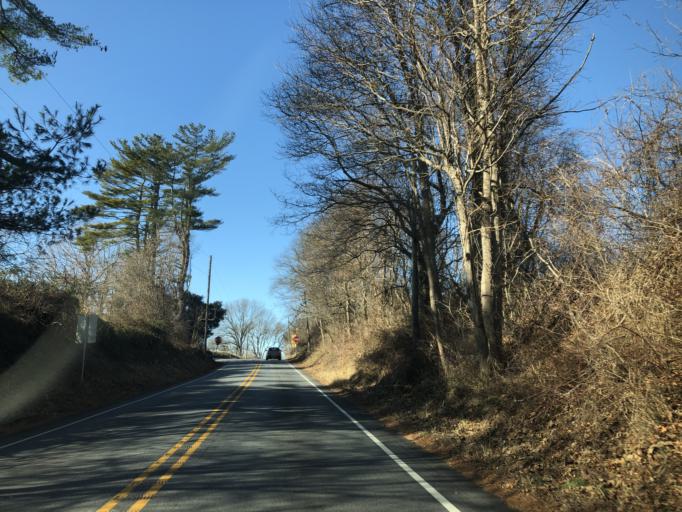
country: US
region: Pennsylvania
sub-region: Chester County
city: Upland
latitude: 39.9022
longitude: -75.7815
